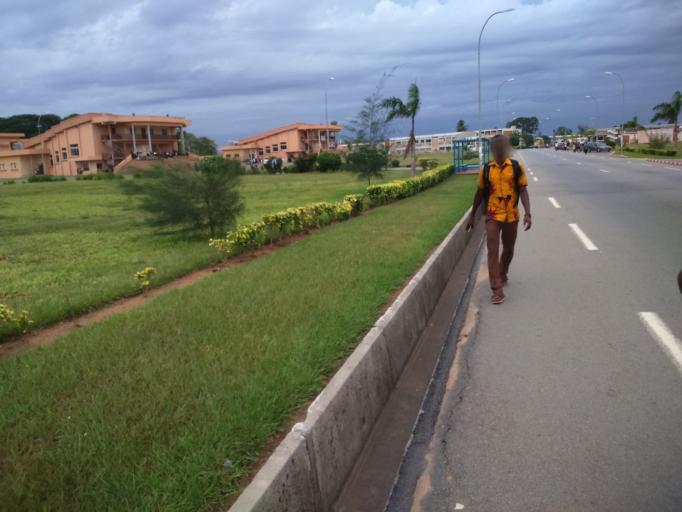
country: CI
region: Lagunes
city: Abidjan
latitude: 5.3481
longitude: -3.9878
